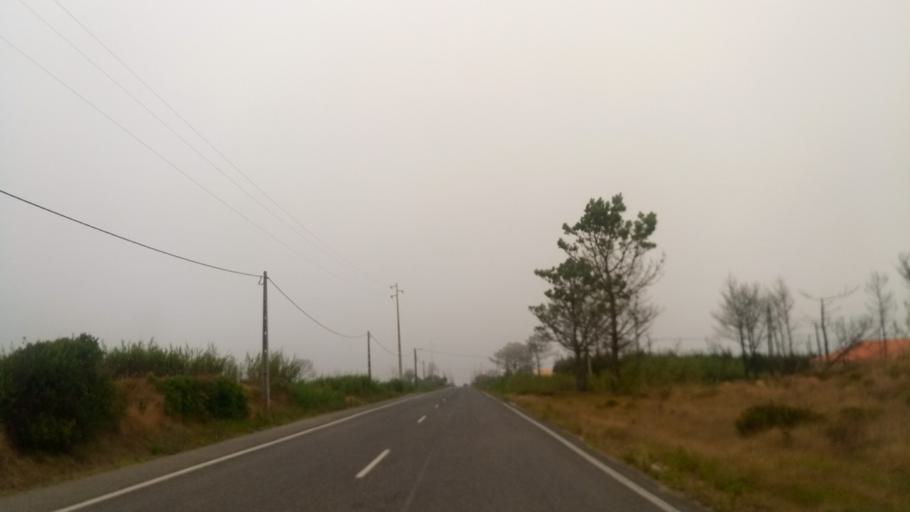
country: PT
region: Leiria
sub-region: Caldas da Rainha
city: Caldas da Rainha
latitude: 39.4601
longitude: -9.1986
